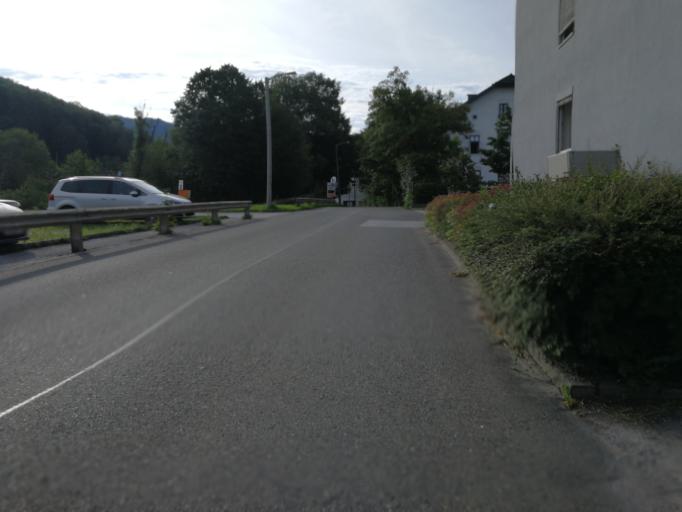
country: AT
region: Salzburg
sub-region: Politischer Bezirk Salzburg-Umgebung
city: Hallwang
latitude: 47.8375
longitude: 13.0625
